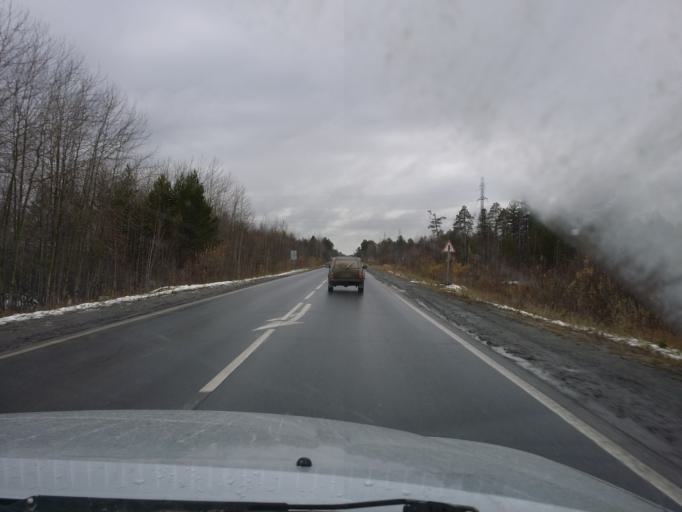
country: RU
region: Khanty-Mansiyskiy Avtonomnyy Okrug
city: Megion
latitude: 61.1257
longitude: 75.8199
